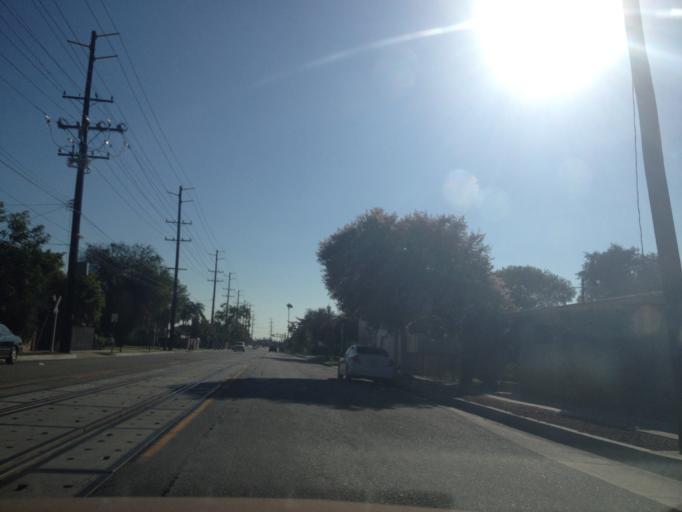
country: US
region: California
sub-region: Orange County
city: Anaheim
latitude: 33.8288
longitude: -117.9227
